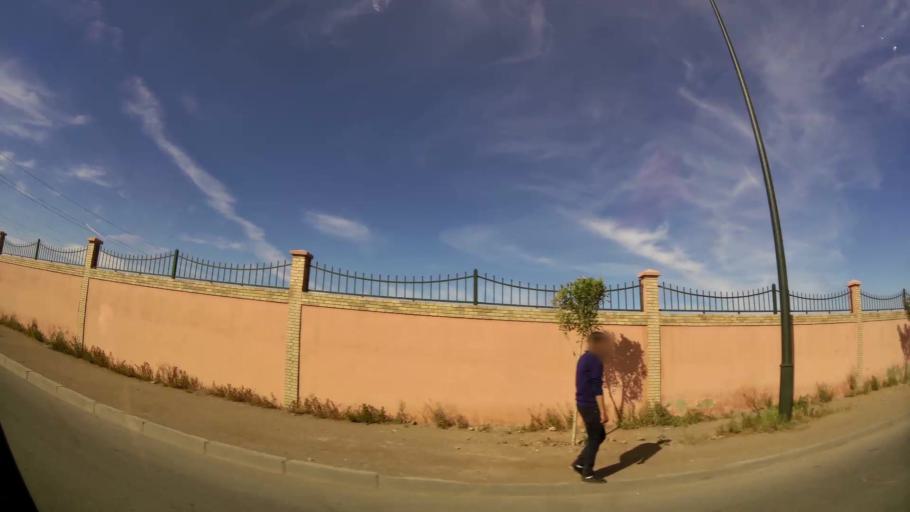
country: MA
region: Marrakech-Tensift-Al Haouz
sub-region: Marrakech
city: Marrakesh
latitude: 31.6602
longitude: -8.0264
